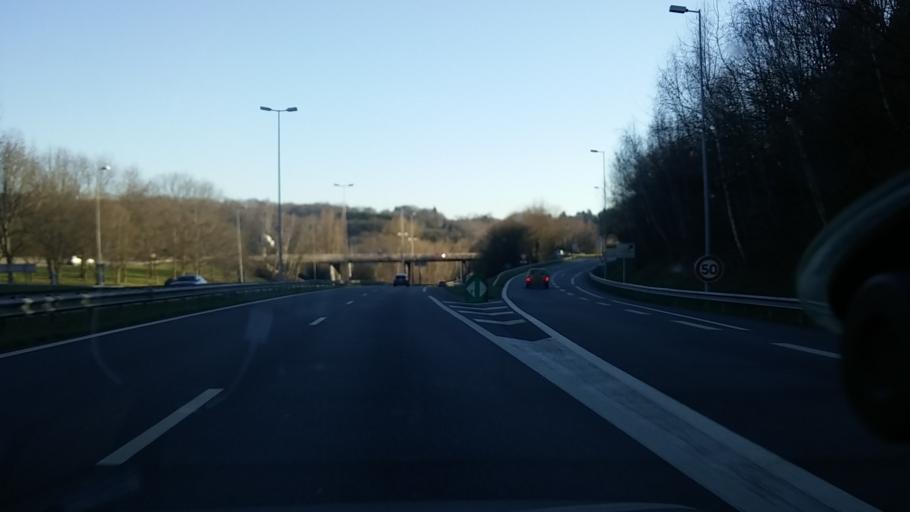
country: FR
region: Limousin
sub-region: Departement de la Haute-Vienne
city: Condat-sur-Vienne
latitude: 45.8089
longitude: 1.2978
